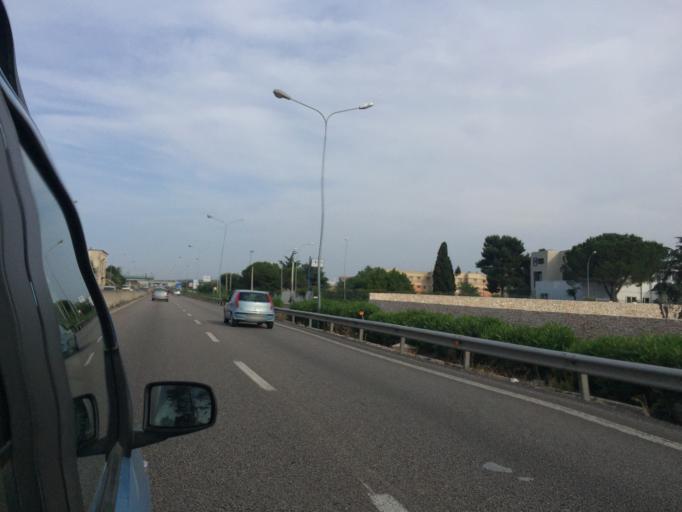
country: IT
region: Apulia
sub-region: Provincia di Bari
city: Triggiano
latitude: 41.0991
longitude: 16.9341
